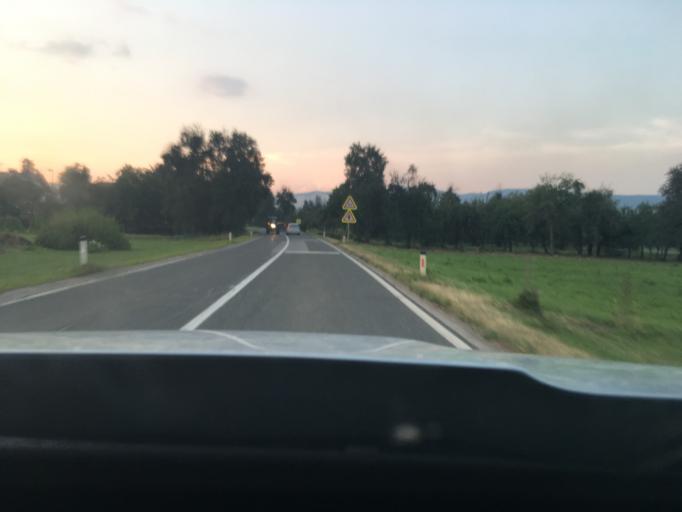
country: SI
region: Ribnica
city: Ribnica
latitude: 45.7061
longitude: 14.7573
